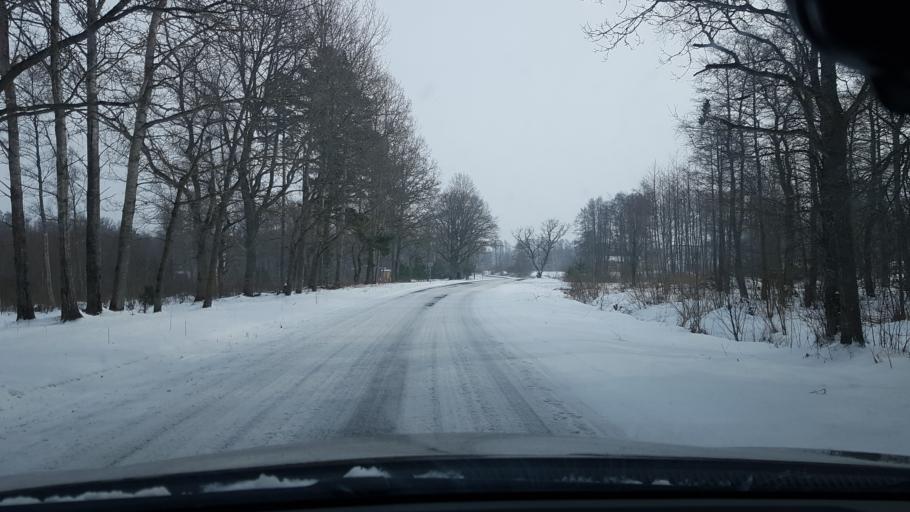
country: EE
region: Harju
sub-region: Kuusalu vald
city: Kuusalu
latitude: 59.4860
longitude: 25.3945
